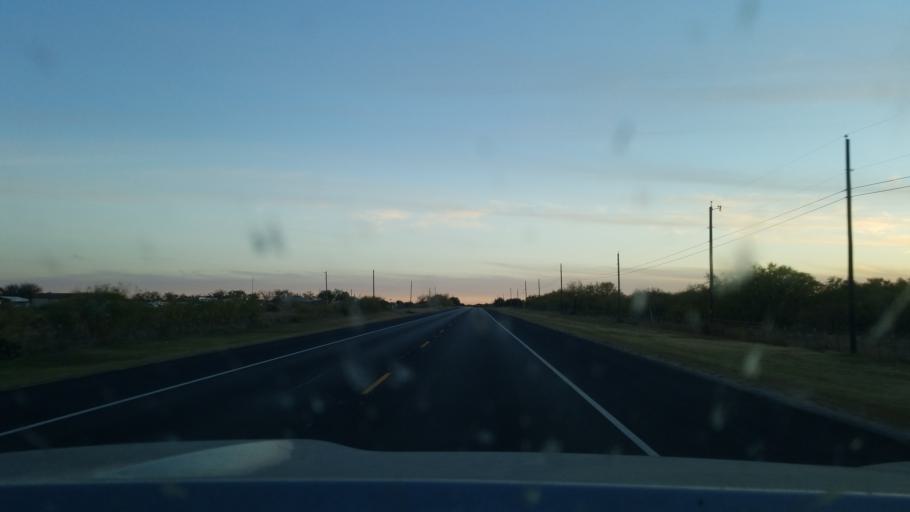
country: US
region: Texas
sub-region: Stephens County
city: Breckenridge
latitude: 32.6334
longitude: -98.9029
